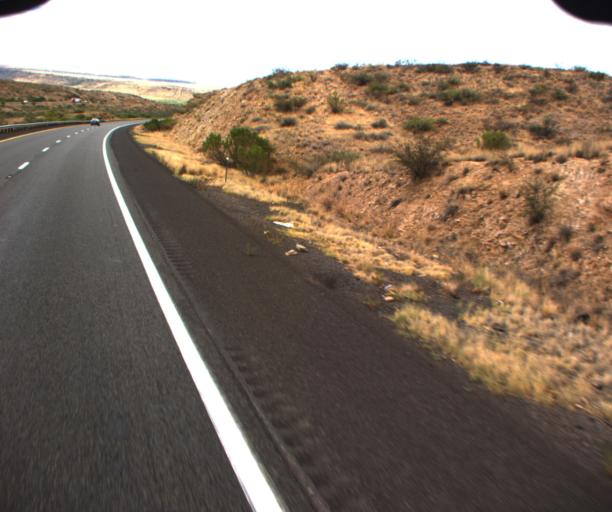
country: US
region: Arizona
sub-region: Yavapai County
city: Cordes Lakes
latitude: 34.2550
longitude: -112.1147
